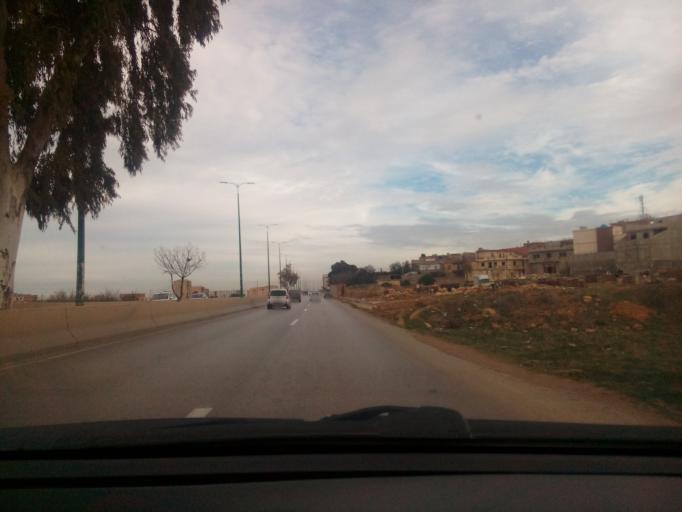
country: DZ
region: Tlemcen
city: Tlemcen
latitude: 34.9047
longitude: -1.3447
